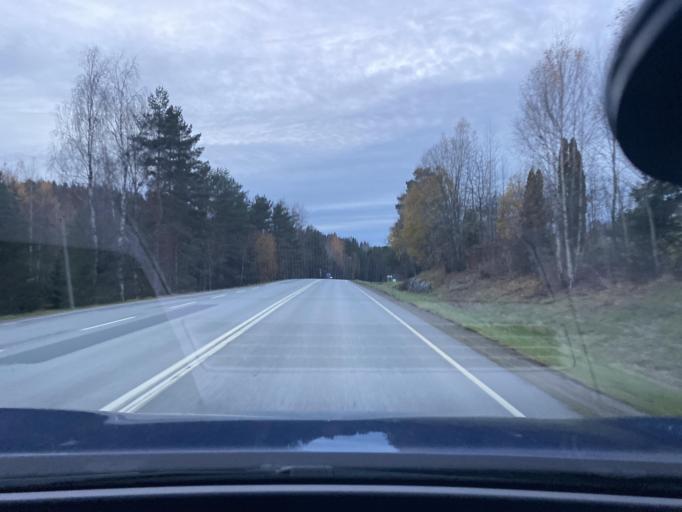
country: FI
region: Uusimaa
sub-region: Helsinki
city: Sammatti
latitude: 60.3844
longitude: 23.8870
